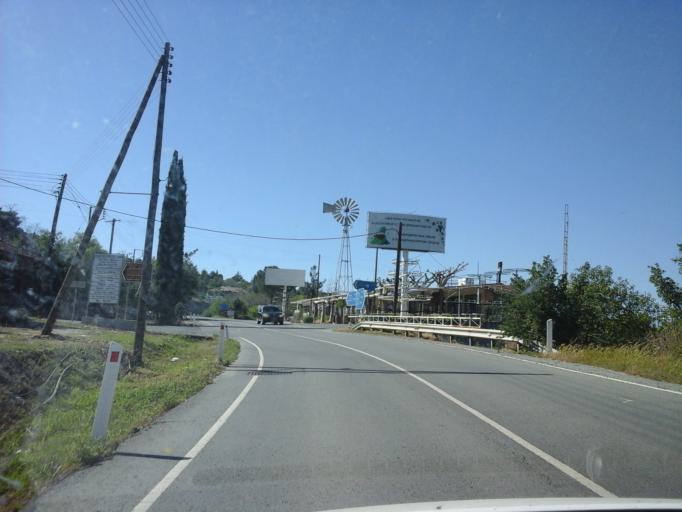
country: CY
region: Limassol
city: Pelendri
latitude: 34.8182
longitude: 32.9156
